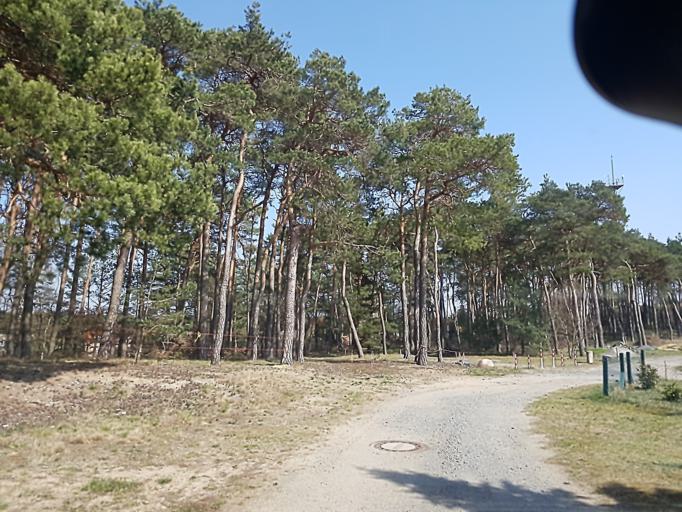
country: DE
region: Brandenburg
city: Bad Liebenwerda
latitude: 51.5401
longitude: 13.4495
